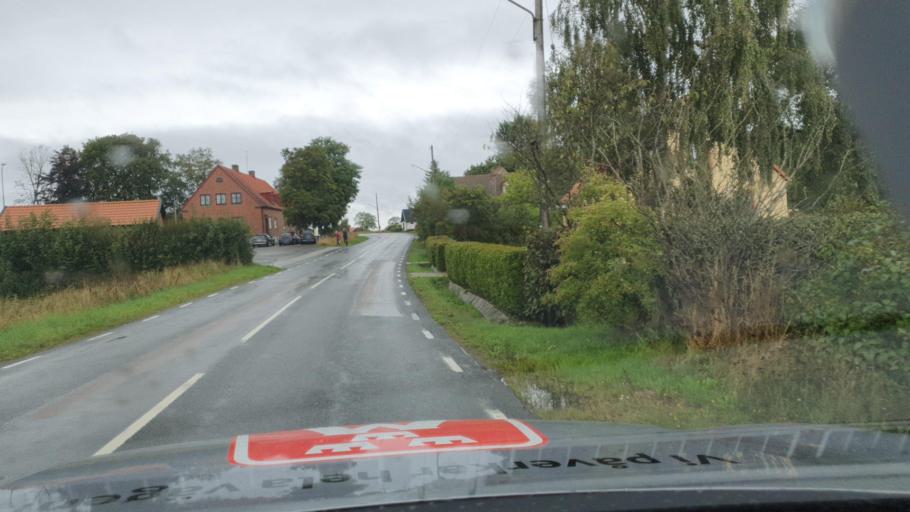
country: SE
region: Skane
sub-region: Simrishamns Kommun
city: Kivik
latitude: 55.5662
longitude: 14.1549
